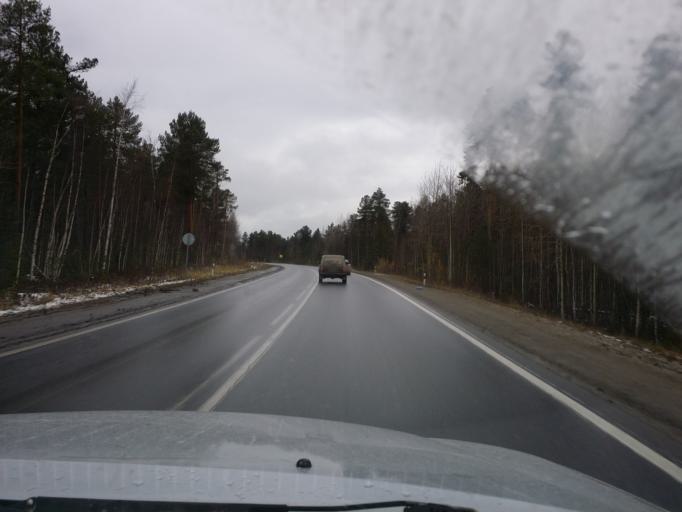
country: RU
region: Khanty-Mansiyskiy Avtonomnyy Okrug
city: Megion
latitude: 61.1229
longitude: 75.8319
